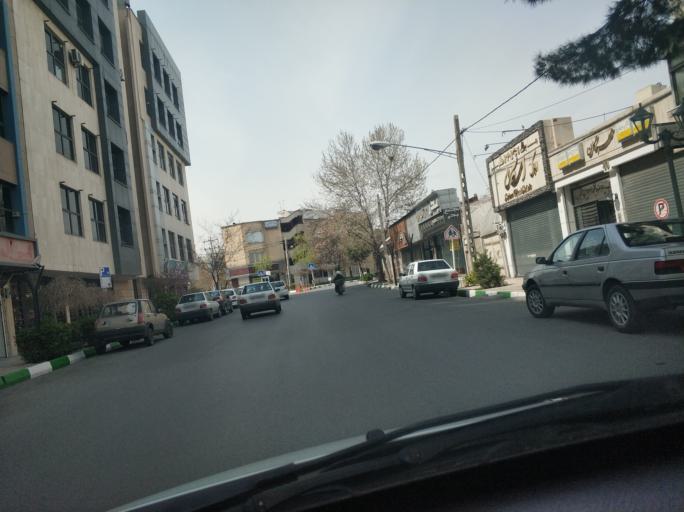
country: IR
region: Razavi Khorasan
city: Mashhad
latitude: 36.3045
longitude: 59.5706
